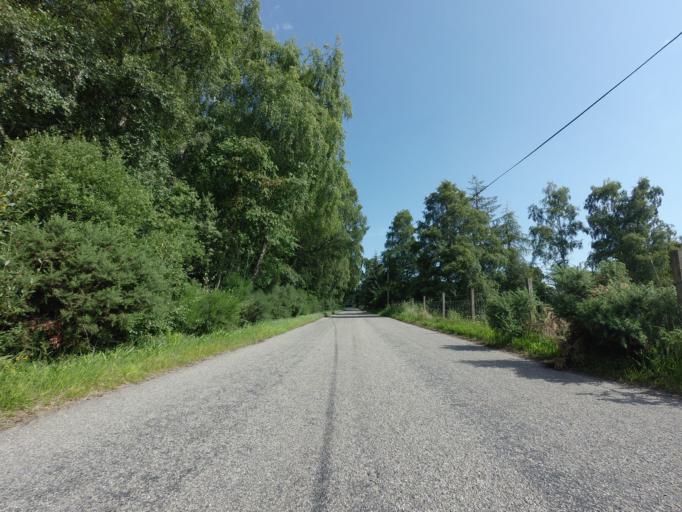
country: GB
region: Scotland
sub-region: Highland
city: Invergordon
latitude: 57.7302
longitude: -4.1928
